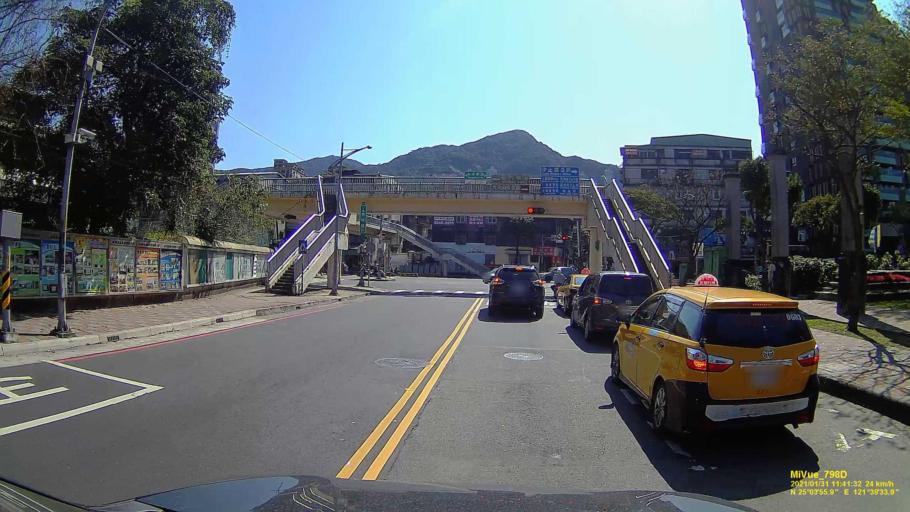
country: TW
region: Taiwan
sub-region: Keelung
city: Keelung
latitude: 25.0655
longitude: 121.6594
